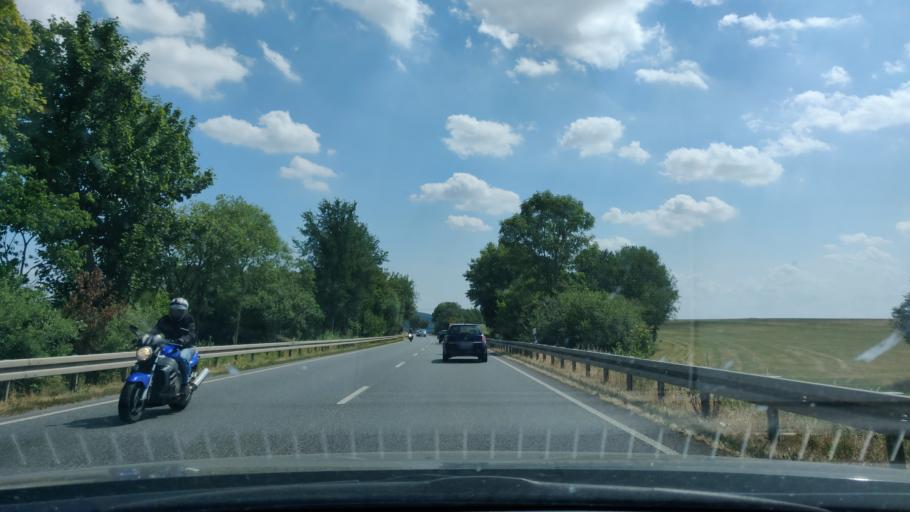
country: DE
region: Hesse
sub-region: Regierungsbezirk Kassel
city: Wabern
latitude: 51.0925
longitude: 9.3375
